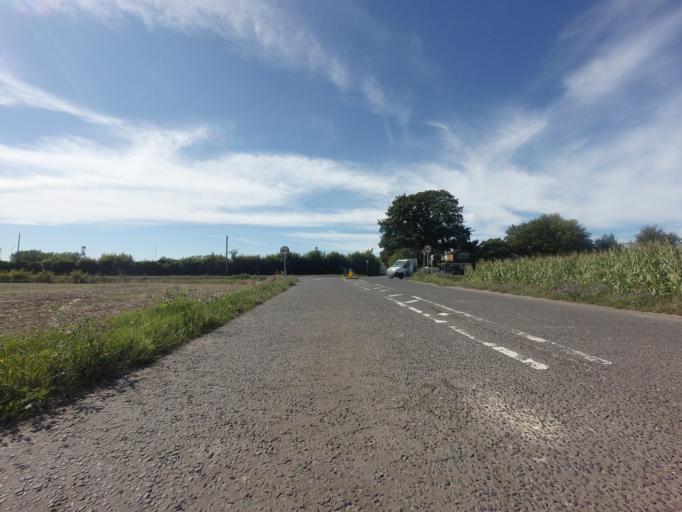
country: GB
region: England
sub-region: Kent
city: Birchington-on-Sea
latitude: 51.3495
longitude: 1.2565
